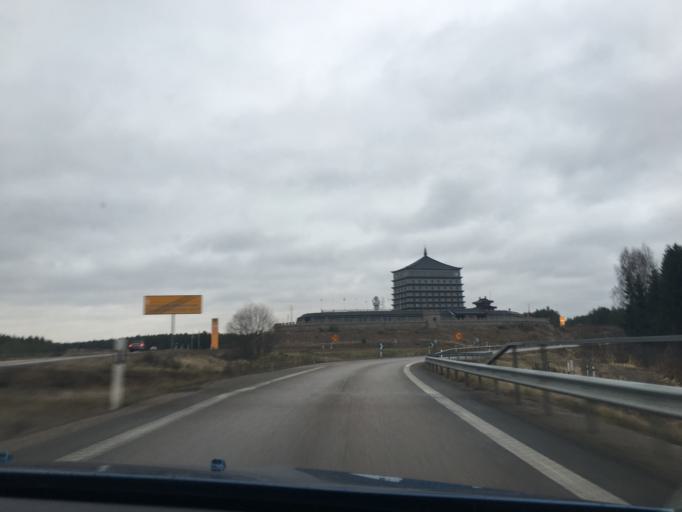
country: SE
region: Uppsala
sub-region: Alvkarleby Kommun
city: AElvkarleby
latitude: 60.4602
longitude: 17.4148
